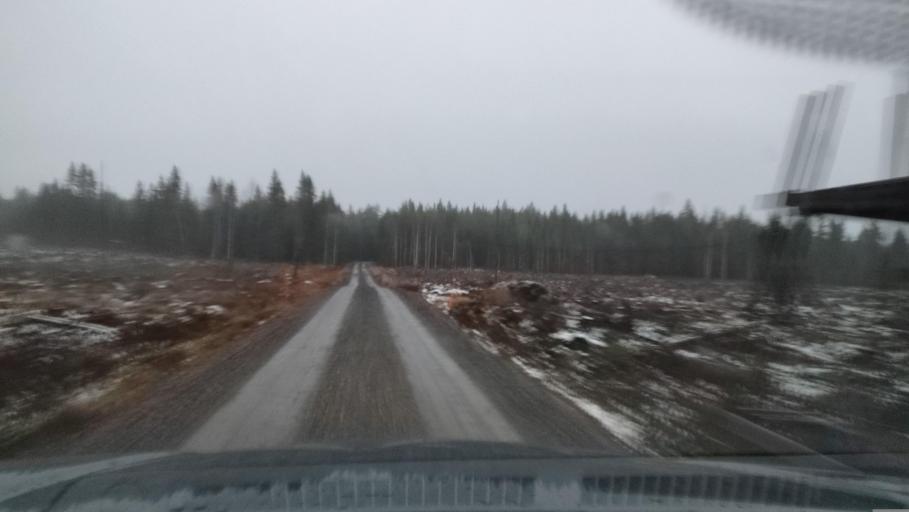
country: FI
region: Southern Ostrobothnia
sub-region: Suupohja
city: Karijoki
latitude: 62.1366
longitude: 21.6269
